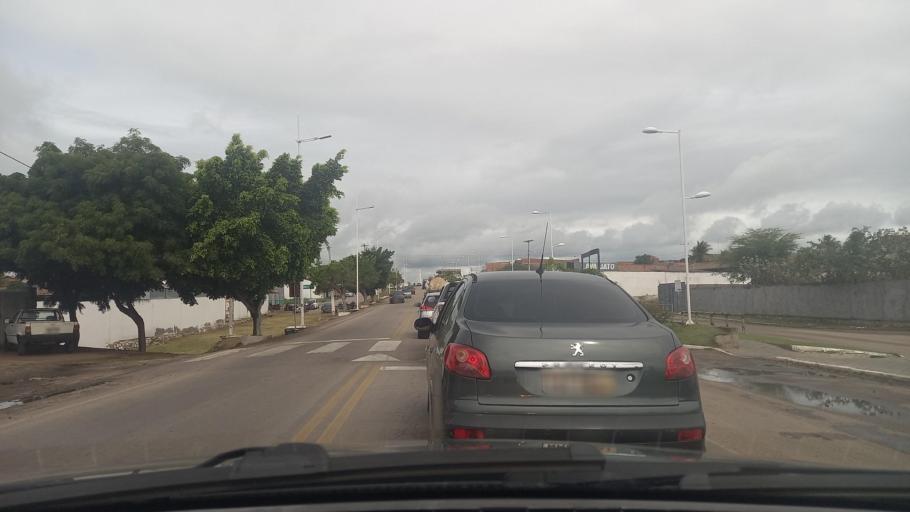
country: BR
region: Bahia
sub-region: Paulo Afonso
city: Paulo Afonso
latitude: -9.4435
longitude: -38.2229
